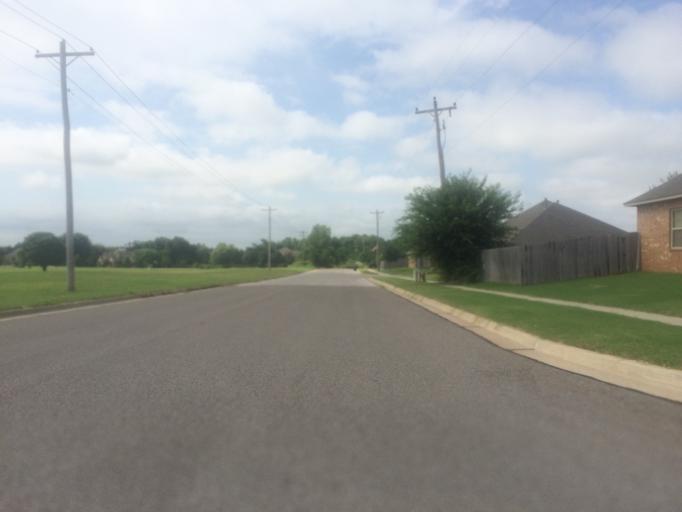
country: US
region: Oklahoma
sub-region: Cleveland County
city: Noble
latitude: 35.1645
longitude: -97.4237
